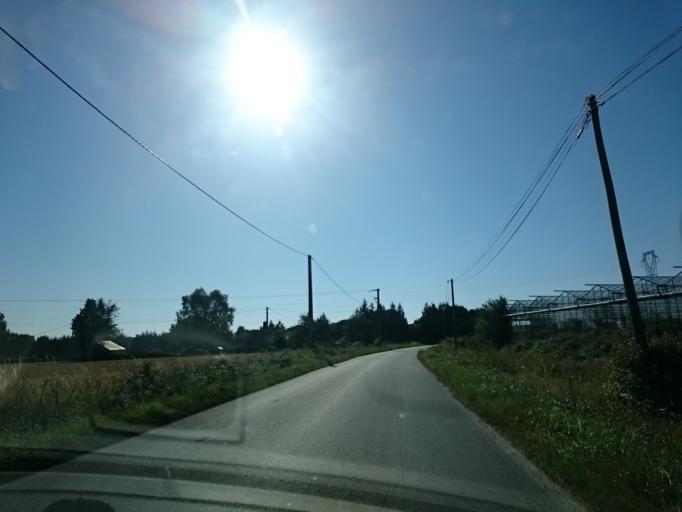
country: FR
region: Brittany
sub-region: Departement d'Ille-et-Vilaine
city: Bourgbarre
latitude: 47.9915
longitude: -1.5974
